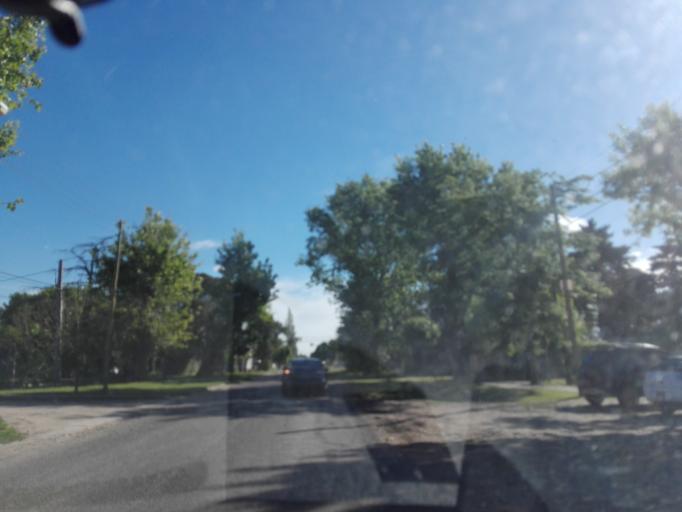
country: AR
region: Buenos Aires
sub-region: Partido de La Plata
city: La Plata
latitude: -34.8964
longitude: -58.0137
